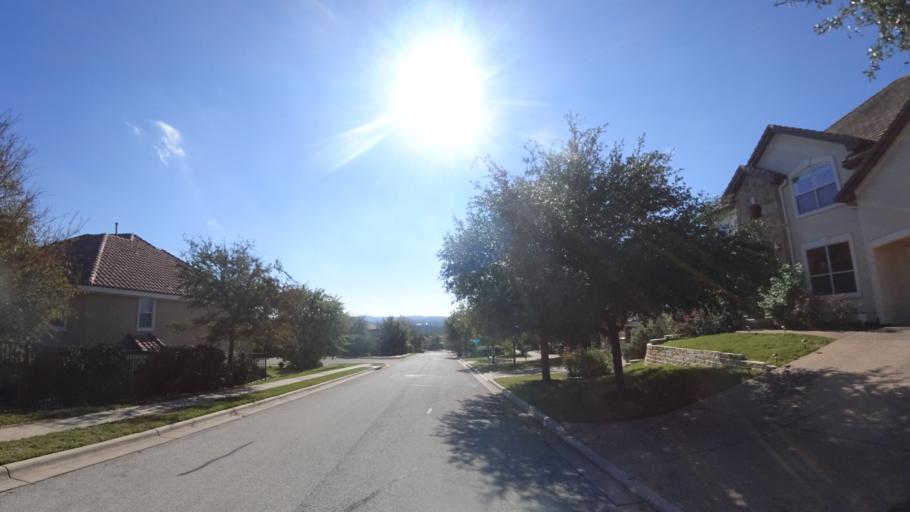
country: US
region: Texas
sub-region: Travis County
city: Hudson Bend
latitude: 30.3592
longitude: -97.8868
